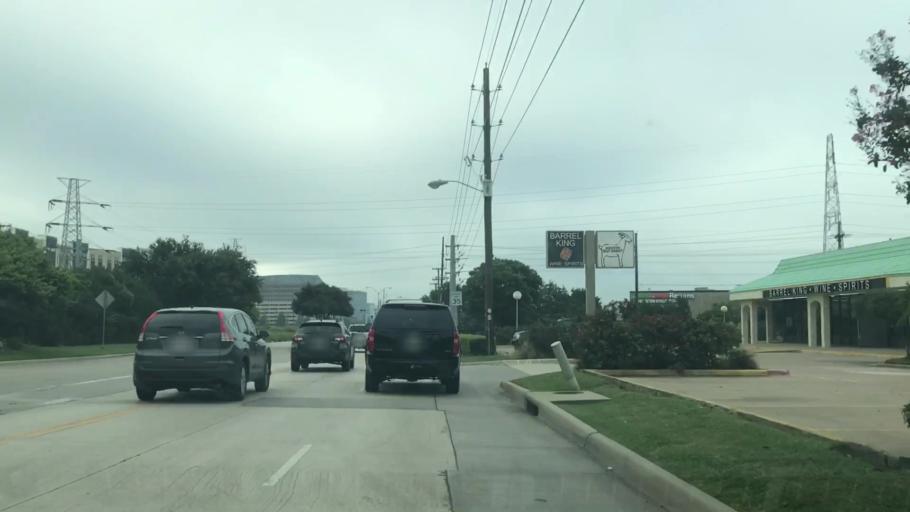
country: US
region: Texas
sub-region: Dallas County
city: Addison
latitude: 32.9477
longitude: -96.8285
